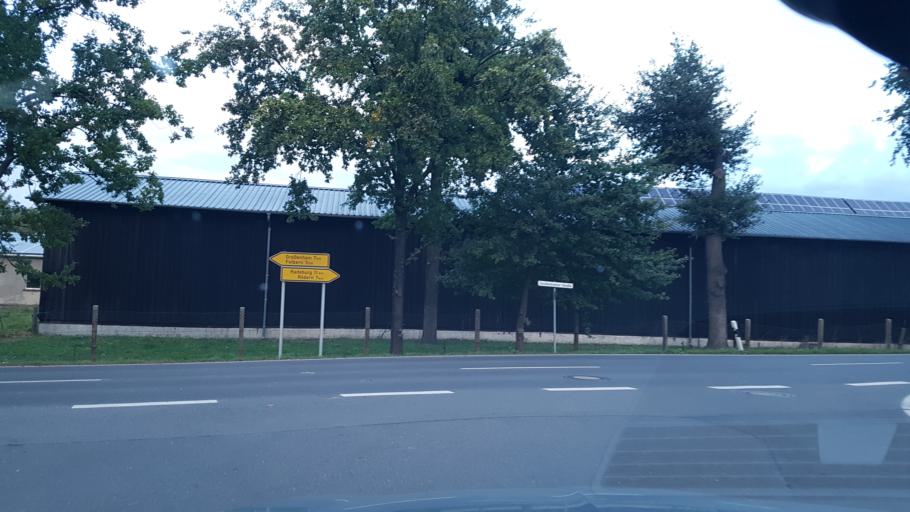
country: DE
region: Saxony
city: Ebersbach
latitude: 51.2792
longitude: 13.6236
